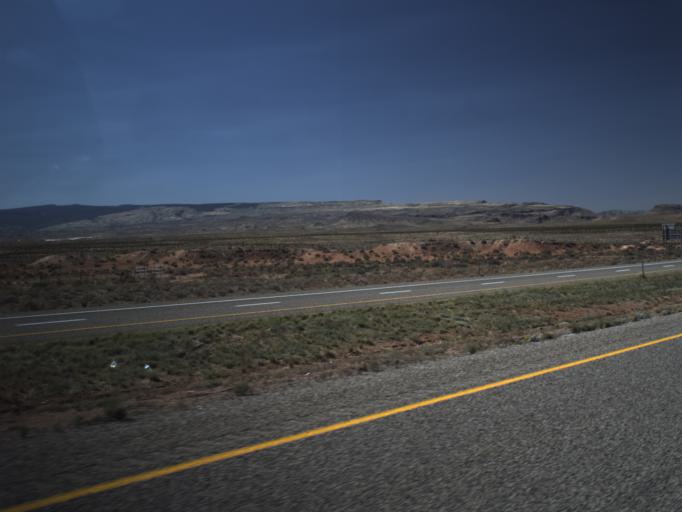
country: US
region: Utah
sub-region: Washington County
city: Saint George
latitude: 37.0009
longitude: -113.5711
